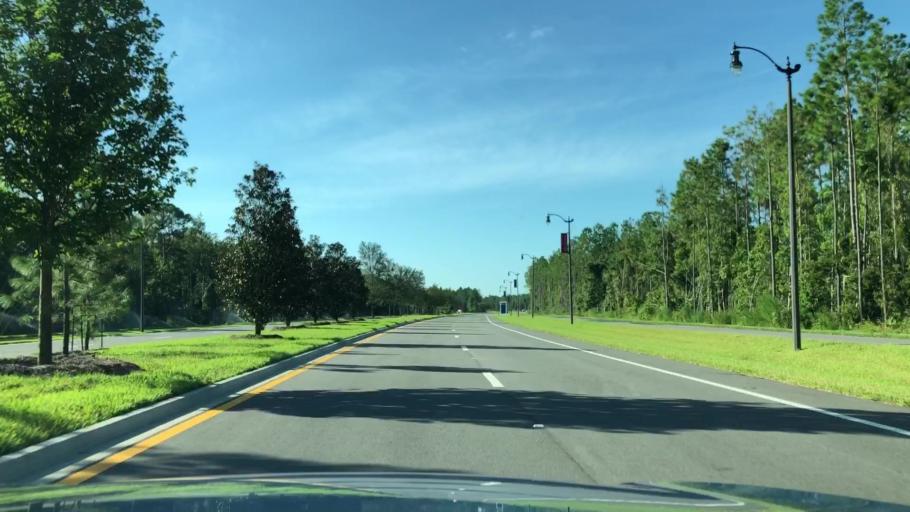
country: US
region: Florida
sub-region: Saint Johns County
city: Palm Valley
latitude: 30.0915
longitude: -81.4069
